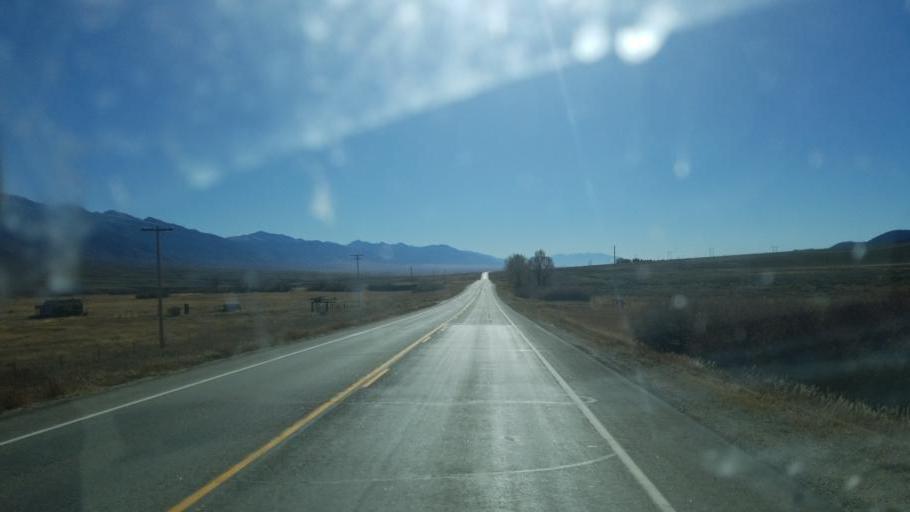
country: US
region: Colorado
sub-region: Chaffee County
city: Salida
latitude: 38.3839
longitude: -106.0526
